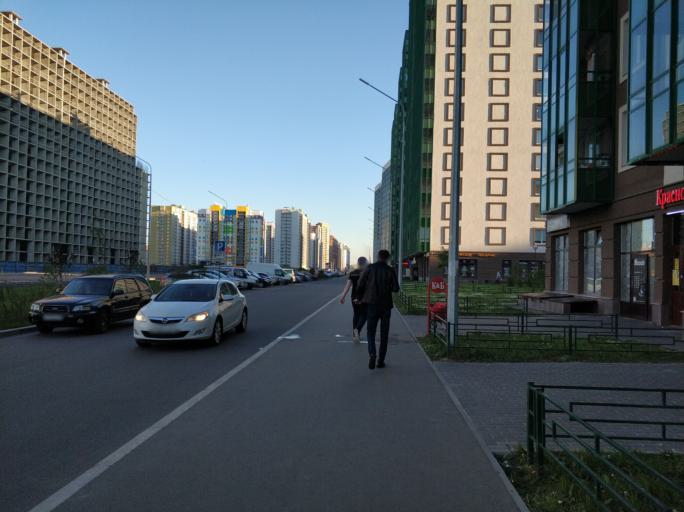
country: RU
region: Leningrad
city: Murino
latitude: 60.0644
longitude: 30.4338
